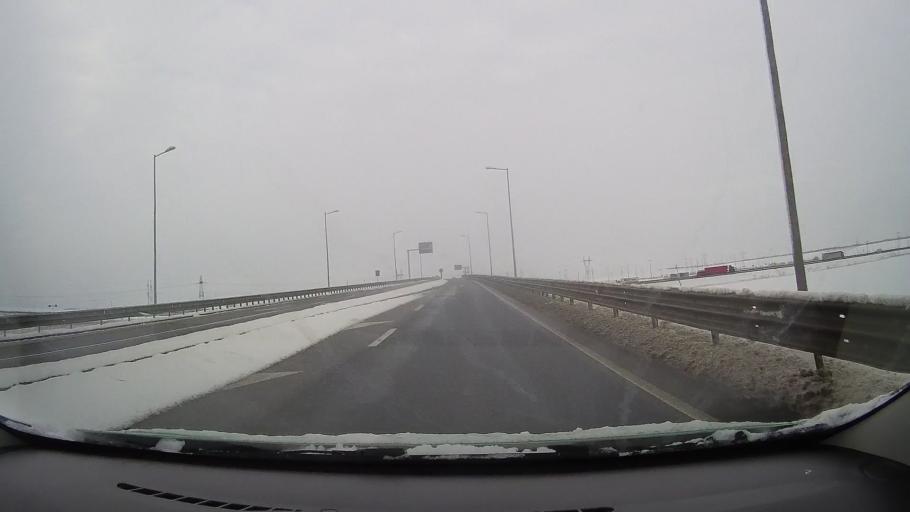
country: RO
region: Alba
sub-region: Municipiul Sebes
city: Lancram
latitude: 45.9754
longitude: 23.5229
